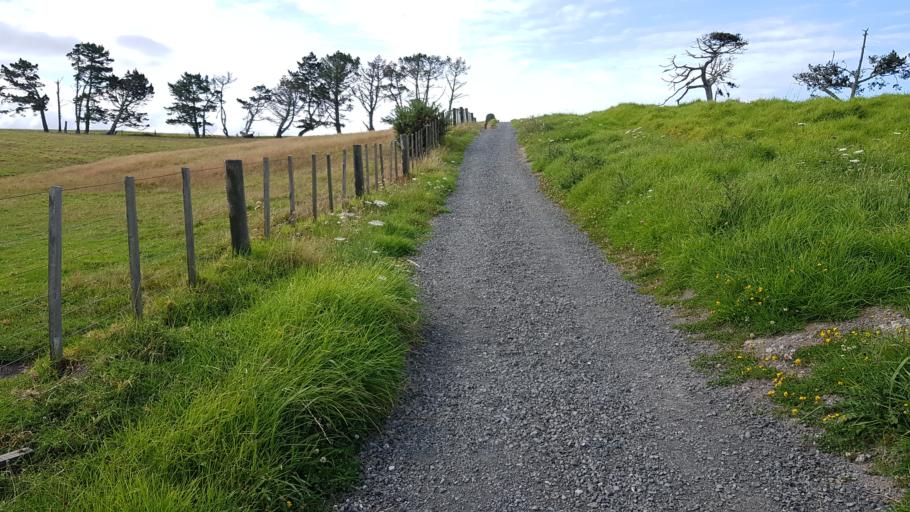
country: NZ
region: Auckland
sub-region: Auckland
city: Rothesay Bay
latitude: -36.6668
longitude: 174.7460
